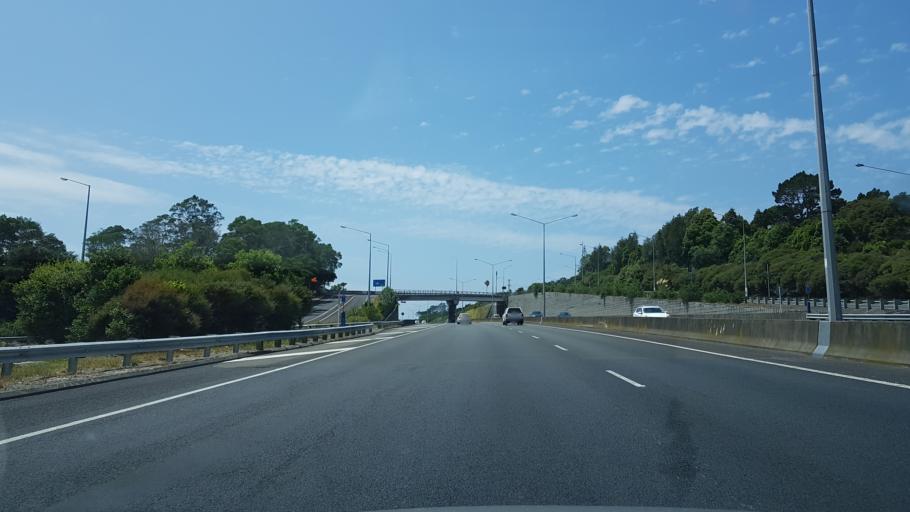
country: NZ
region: Auckland
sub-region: Auckland
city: North Shore
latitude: -36.7828
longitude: 174.6749
